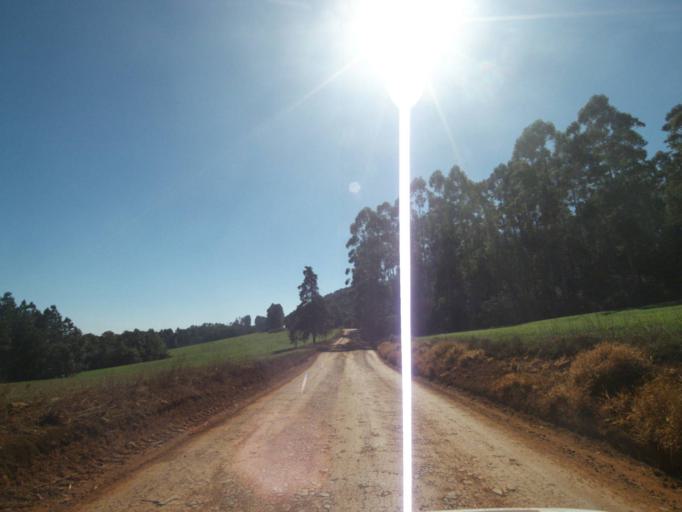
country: BR
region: Parana
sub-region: Tibagi
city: Tibagi
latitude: -24.5966
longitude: -50.6024
